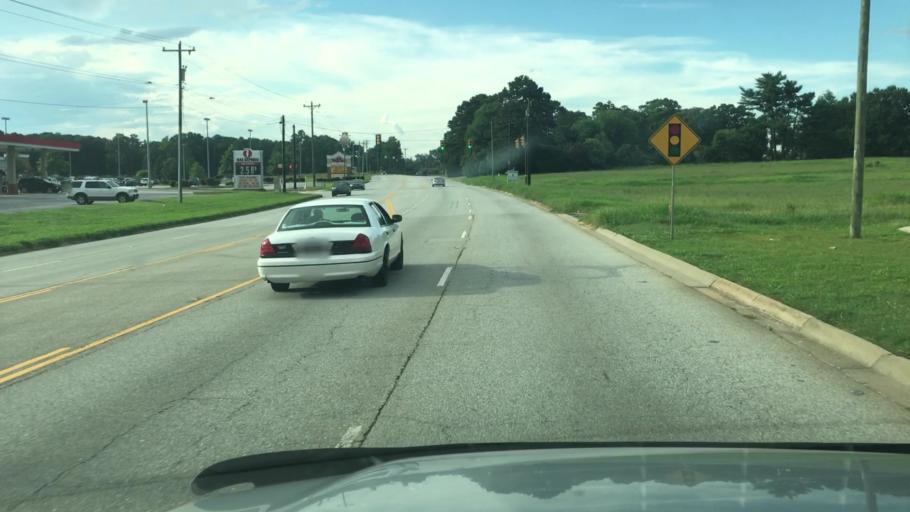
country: US
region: South Carolina
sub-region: Spartanburg County
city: Mayo
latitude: 35.0254
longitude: -81.8954
